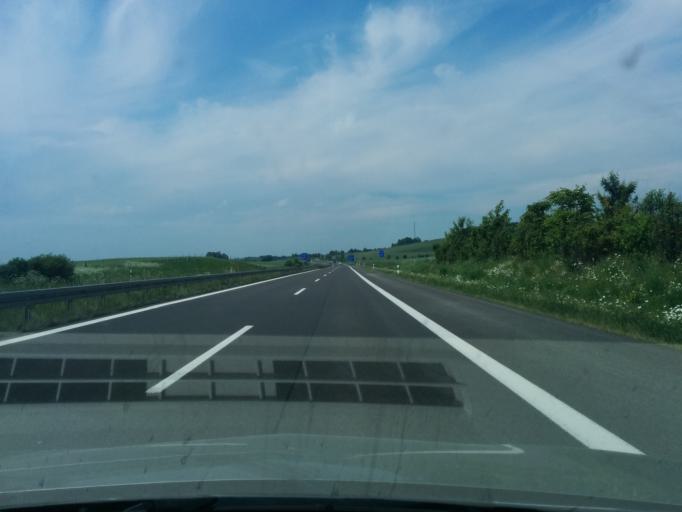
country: DE
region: Mecklenburg-Vorpommern
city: Strasburg
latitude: 53.5381
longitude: 13.7215
